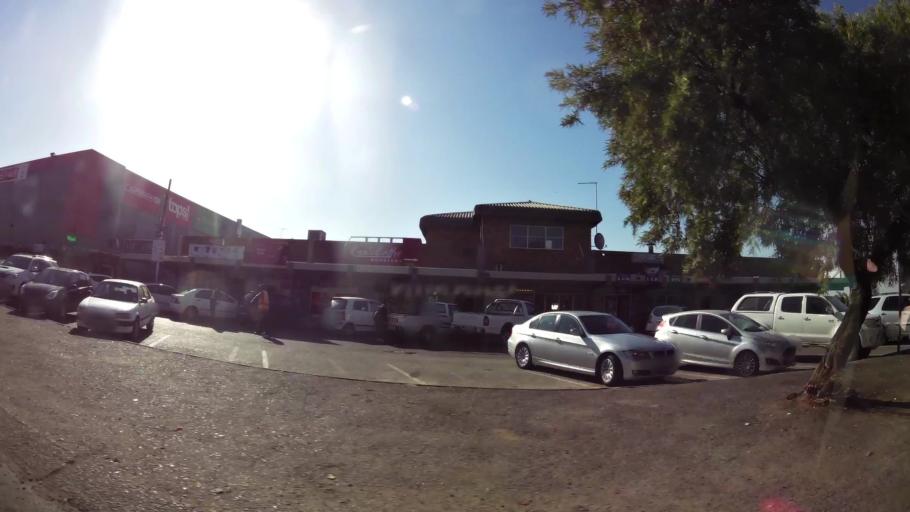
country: ZA
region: Gauteng
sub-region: City of Tshwane Metropolitan Municipality
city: Pretoria
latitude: -25.7206
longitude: 28.2598
